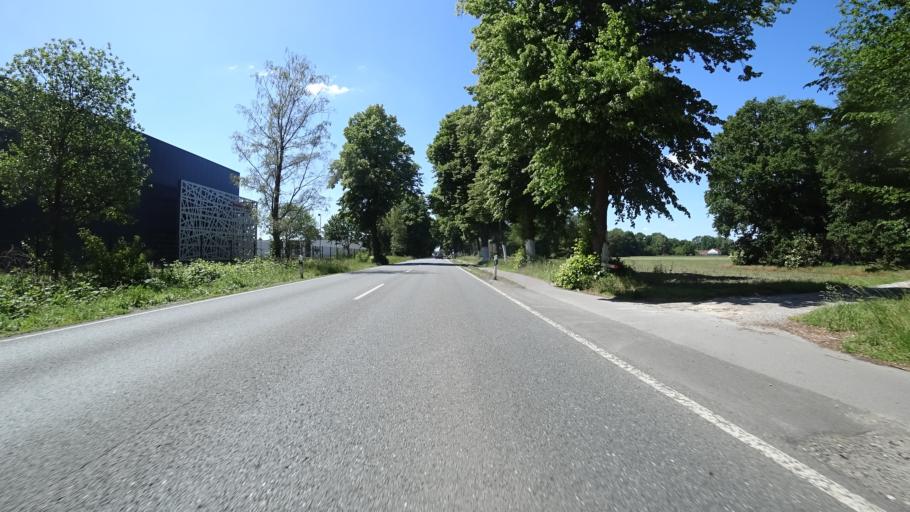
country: DE
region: North Rhine-Westphalia
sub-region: Regierungsbezirk Detmold
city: Guetersloh
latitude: 51.9248
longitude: 8.4037
